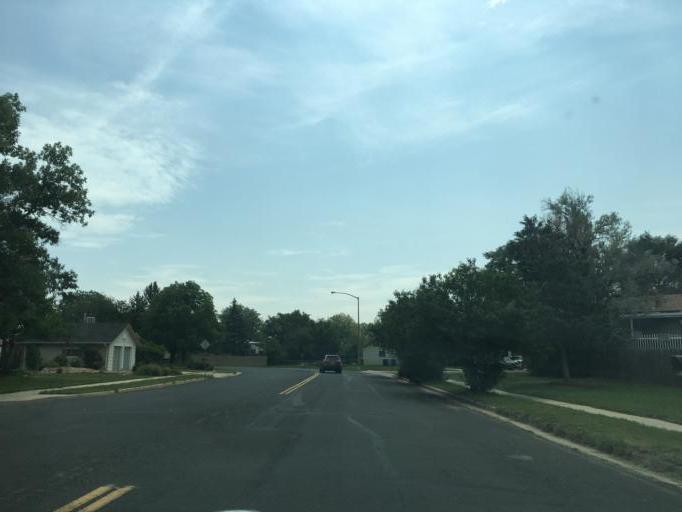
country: US
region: Colorado
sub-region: Adams County
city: Aurora
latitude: 39.7335
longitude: -104.7947
